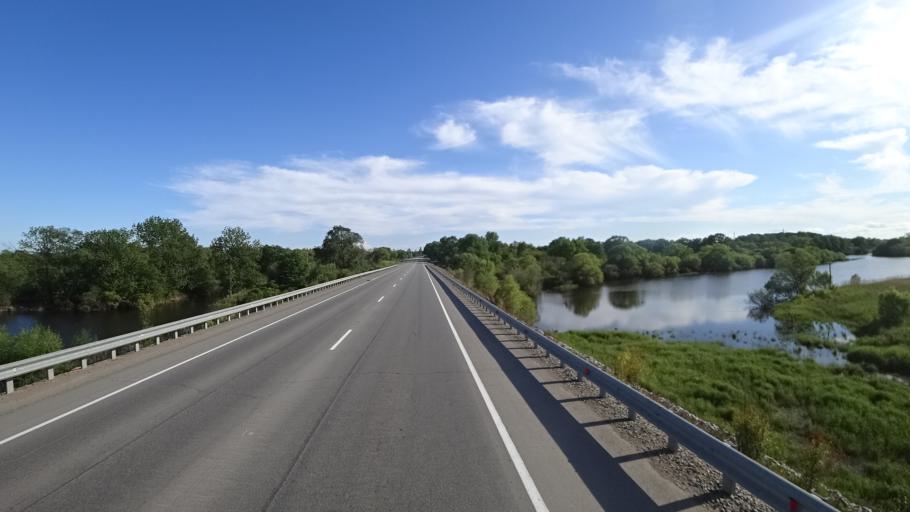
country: RU
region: Khabarovsk Krai
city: Khor
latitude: 47.8605
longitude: 134.9629
